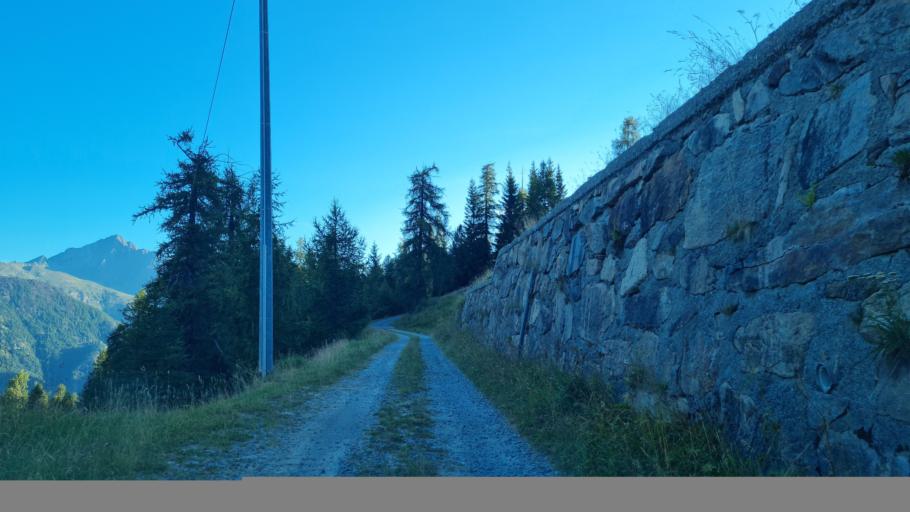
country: IT
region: Aosta Valley
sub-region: Valle d'Aosta
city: Fontainemore
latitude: 45.6271
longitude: 7.8698
